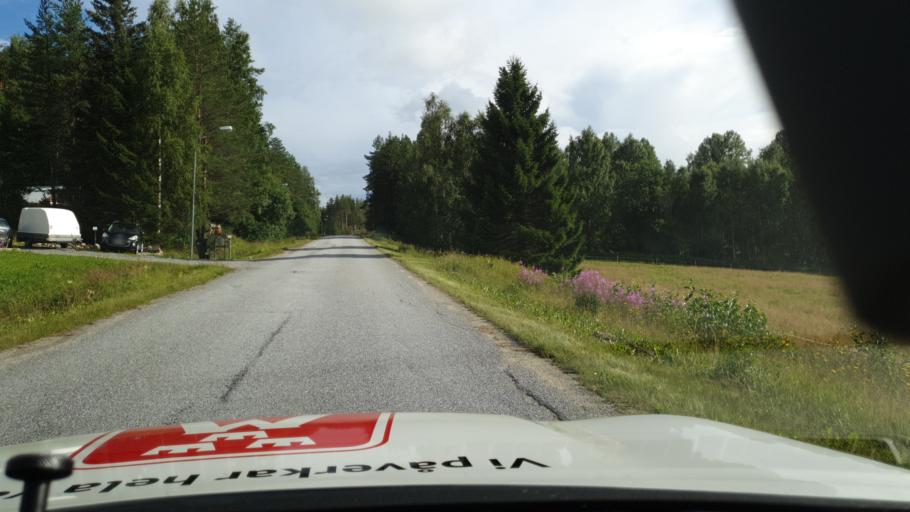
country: SE
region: Vaesterbotten
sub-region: Skelleftea Kommun
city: Burea
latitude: 64.4892
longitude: 21.0336
